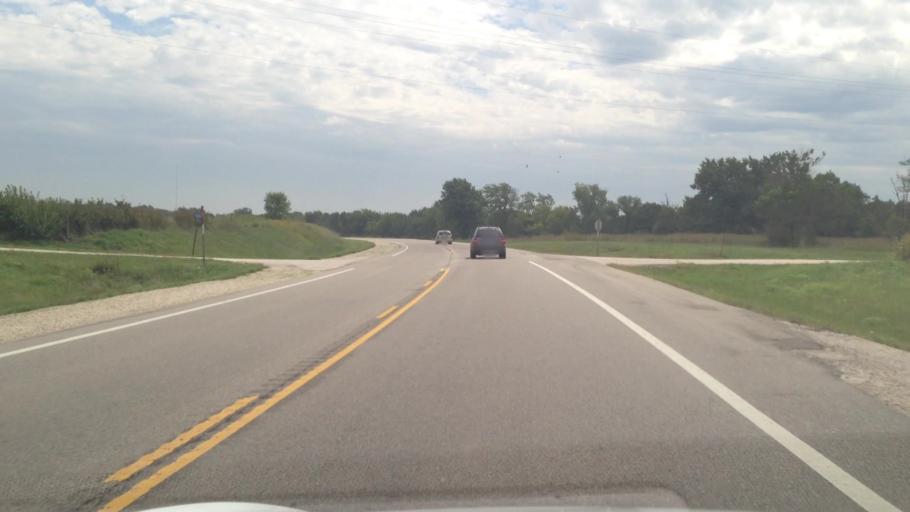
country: US
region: Kansas
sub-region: Allen County
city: Iola
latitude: 37.9160
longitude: -95.1523
